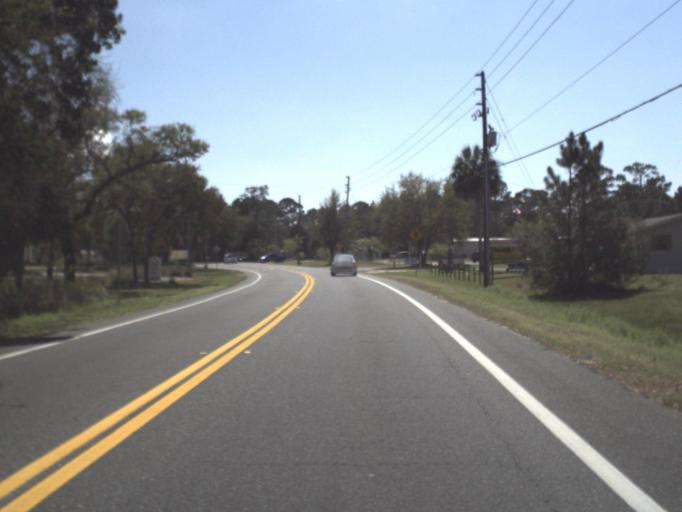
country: US
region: Florida
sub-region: Wakulla County
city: Crawfordville
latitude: 30.0339
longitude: -84.3899
